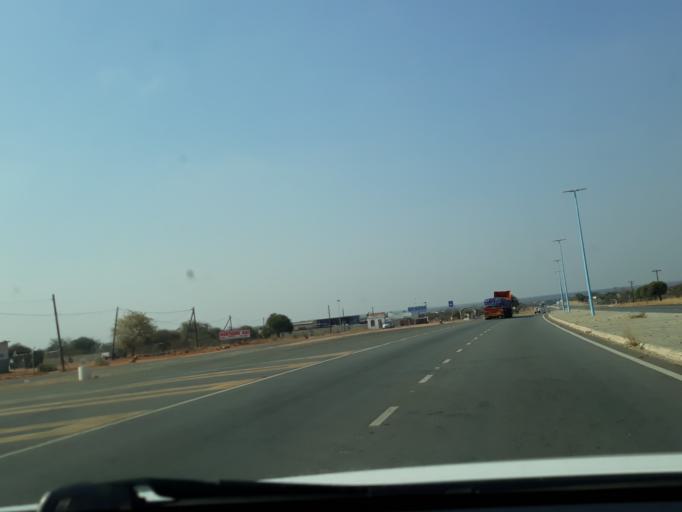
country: BW
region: Central
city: Tonota
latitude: -21.4215
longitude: 27.4432
